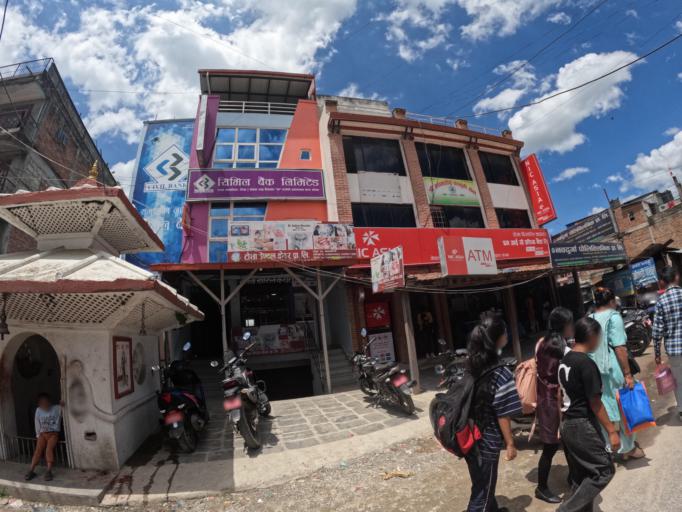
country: NP
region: Central Region
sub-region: Bagmati Zone
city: Kathmandu
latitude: 27.7658
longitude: 85.3305
